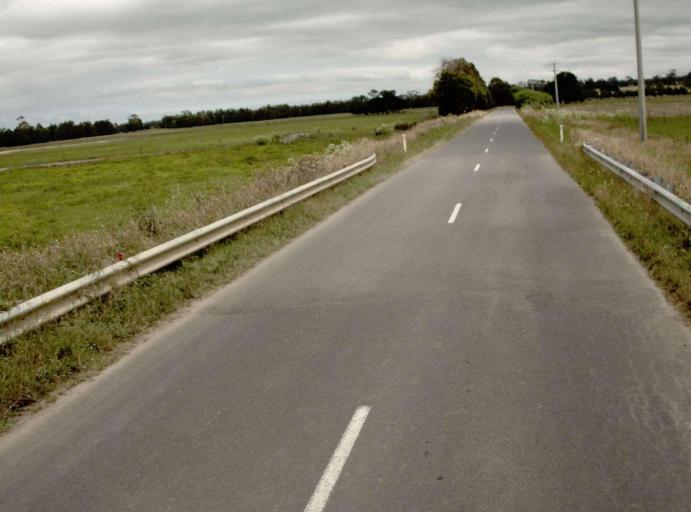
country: AU
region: Victoria
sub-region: Latrobe
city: Traralgon
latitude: -38.5017
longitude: 146.6696
